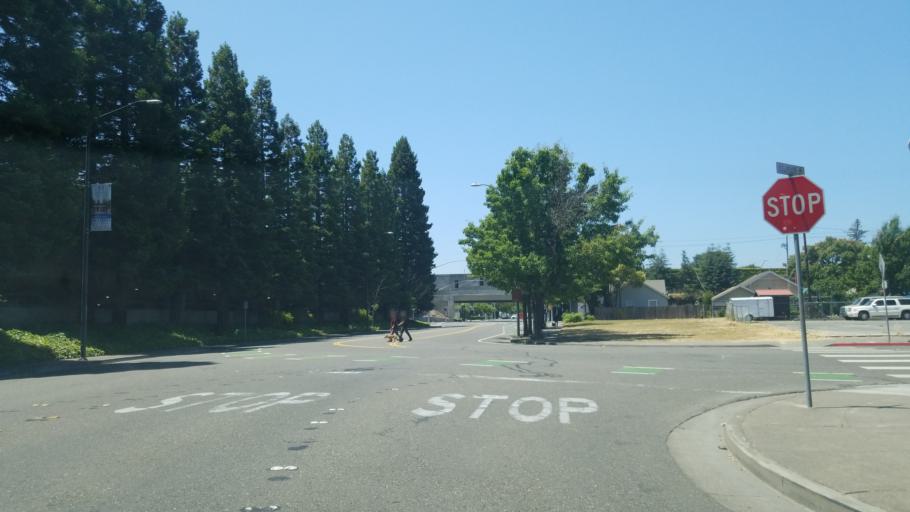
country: US
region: California
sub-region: Sonoma County
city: Santa Rosa
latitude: 38.4406
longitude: -122.7181
